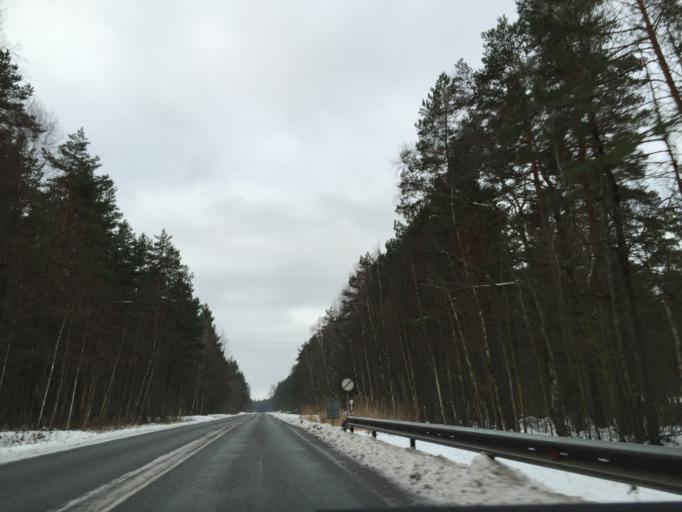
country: LV
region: Saulkrastu
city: Saulkrasti
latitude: 57.2242
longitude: 24.3905
